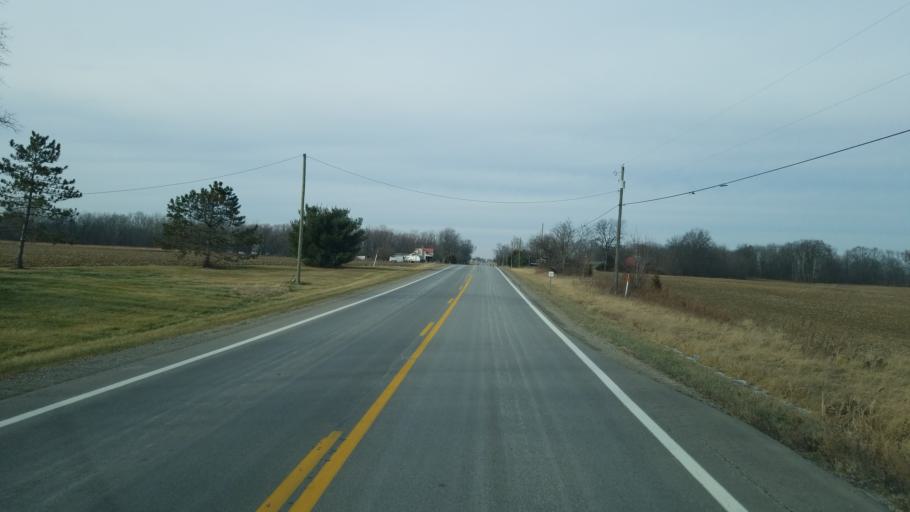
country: US
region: Ohio
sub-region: Hardin County
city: Kenton
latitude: 40.4996
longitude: -83.4935
